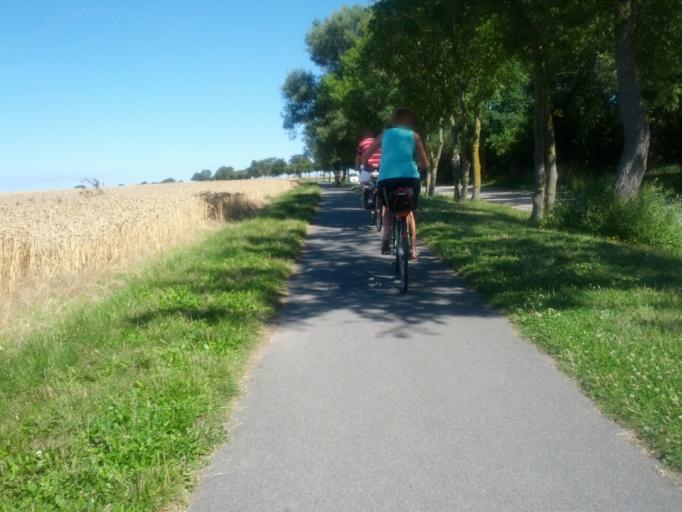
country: DE
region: Mecklenburg-Vorpommern
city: Bastorf
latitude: 54.1146
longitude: 11.6333
